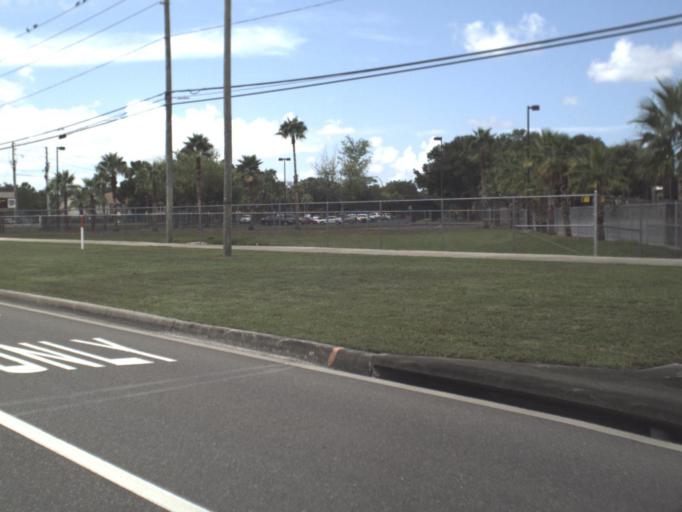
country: US
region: Florida
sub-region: Pinellas County
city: Safety Harbor
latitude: 28.0243
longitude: -82.7091
